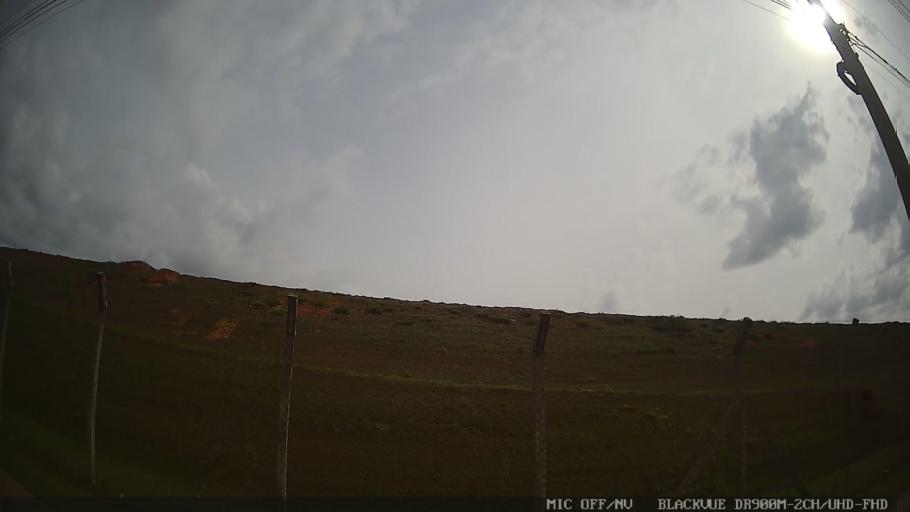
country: BR
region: Sao Paulo
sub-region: Indaiatuba
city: Indaiatuba
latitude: -23.1085
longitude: -47.2783
